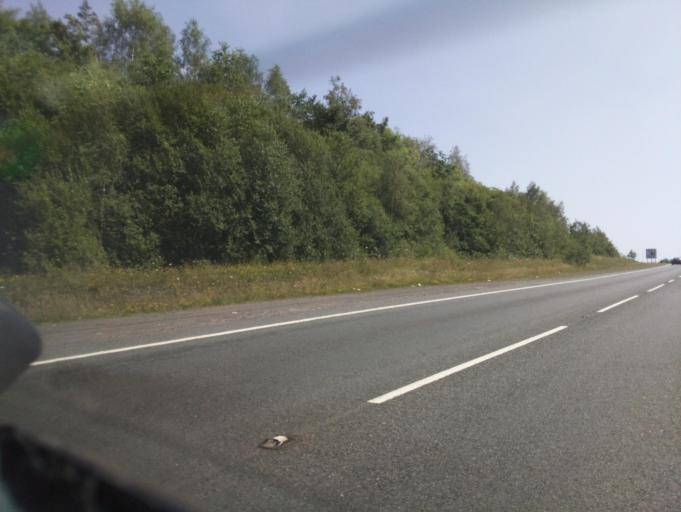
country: GB
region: Wales
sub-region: Caerphilly County Borough
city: Bargoed
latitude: 51.6874
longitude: -3.2254
